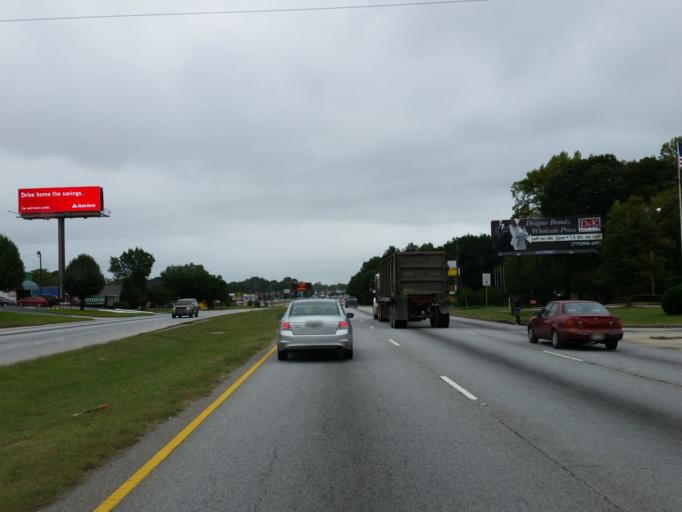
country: US
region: Georgia
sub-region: Clayton County
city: Riverdale
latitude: 33.5823
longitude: -84.3772
